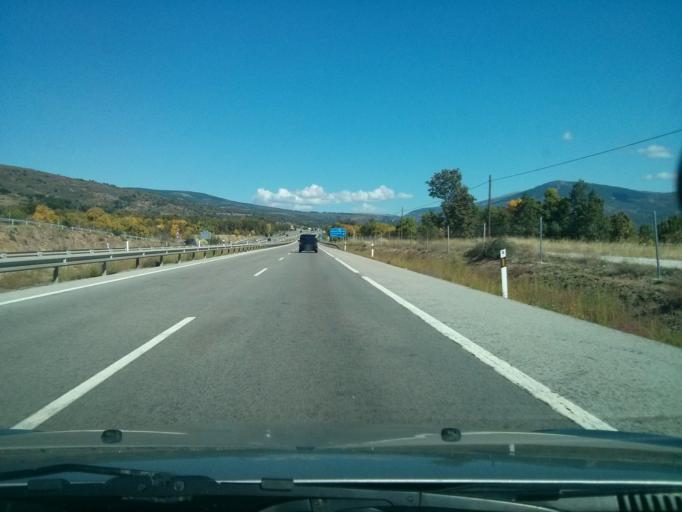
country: ES
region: Madrid
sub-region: Provincia de Madrid
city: Braojos
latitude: 41.0474
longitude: -3.6157
